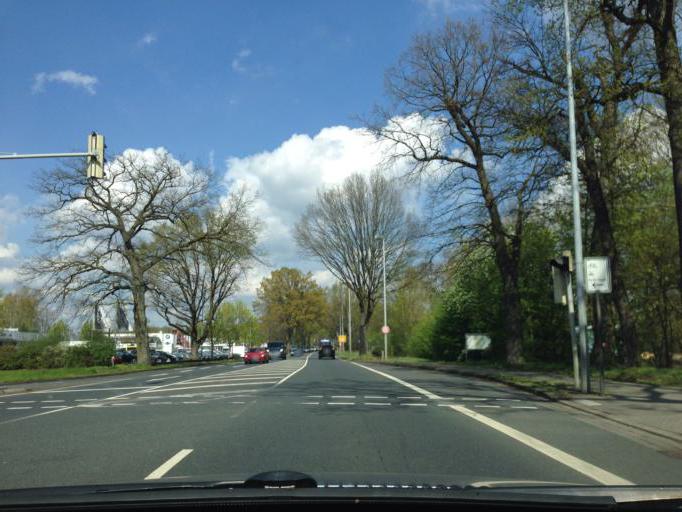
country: DE
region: Lower Saxony
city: Adelheidsdorf
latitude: 52.5894
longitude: 10.0674
